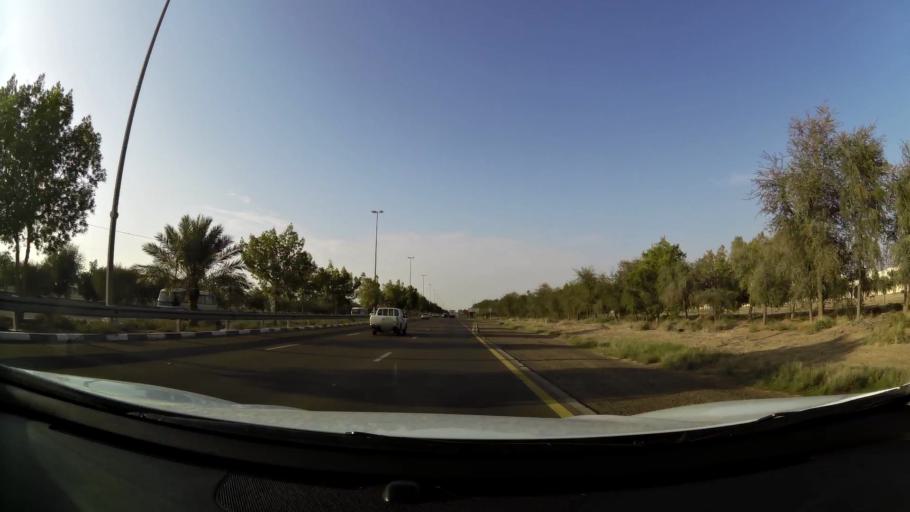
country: AE
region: Abu Dhabi
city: Al Ain
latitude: 24.1040
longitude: 55.8274
